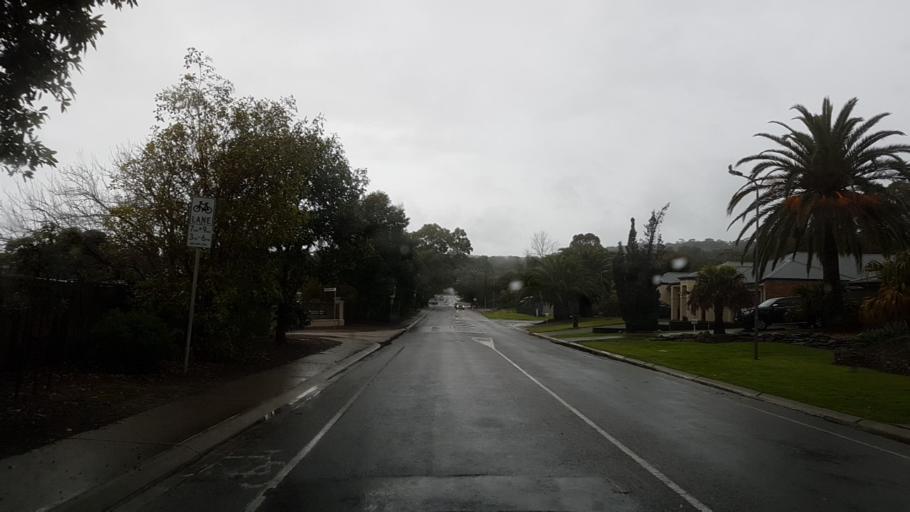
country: AU
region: South Australia
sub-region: Onkaparinga
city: Craigburn Farm
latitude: -35.0809
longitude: 138.5881
